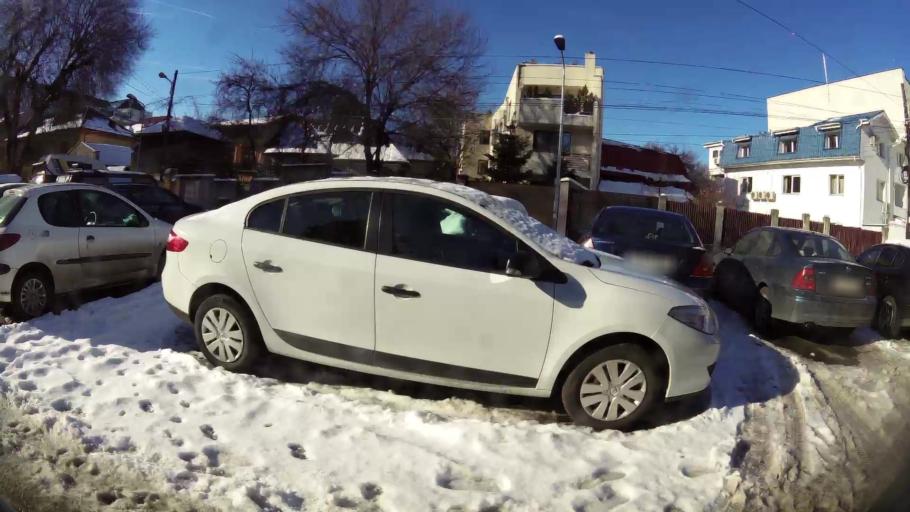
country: RO
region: Bucuresti
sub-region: Municipiul Bucuresti
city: Bucharest
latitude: 44.4171
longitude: 26.1093
